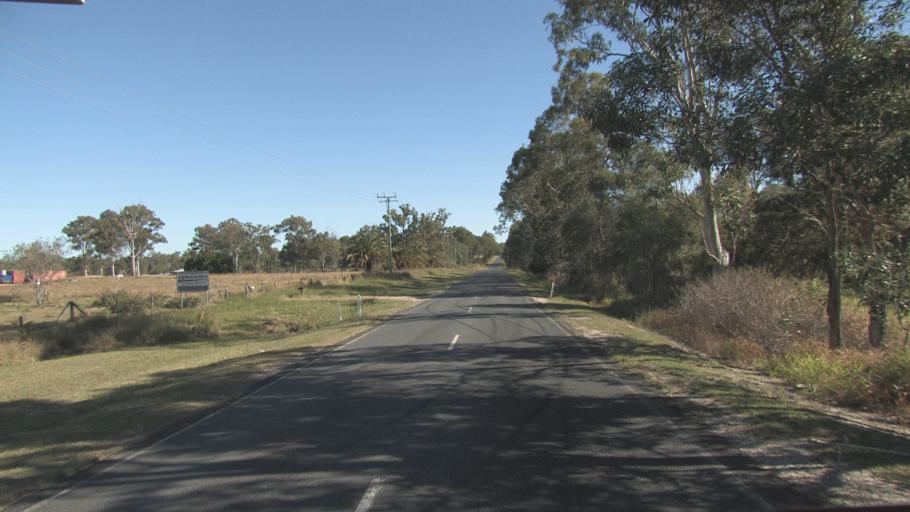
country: AU
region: Queensland
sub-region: Logan
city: North Maclean
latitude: -27.7846
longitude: 153.0505
